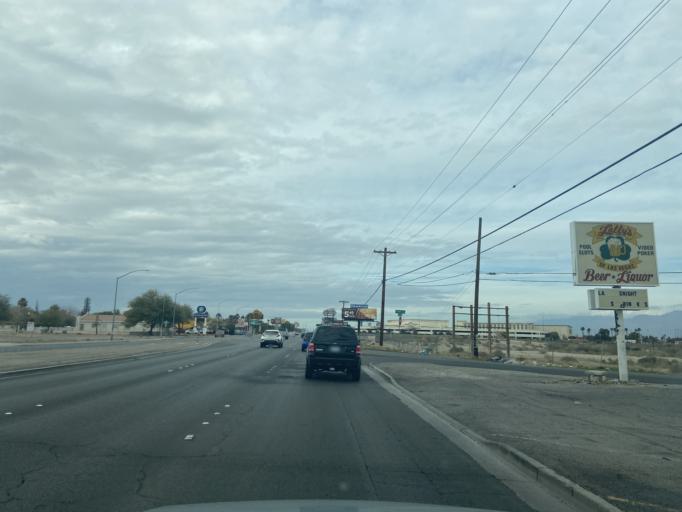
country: US
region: Nevada
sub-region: Clark County
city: Las Vegas
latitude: 36.1918
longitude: -115.1888
